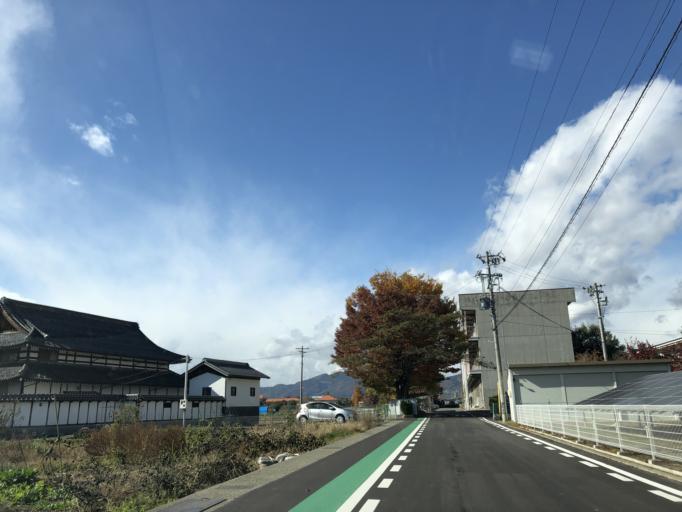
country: JP
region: Nagano
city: Suzaka
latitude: 36.6650
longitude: 138.2563
